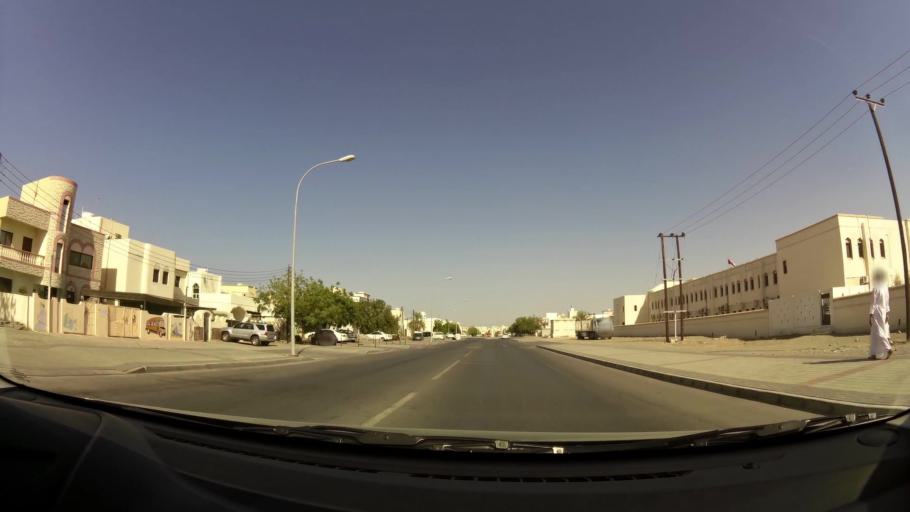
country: OM
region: Muhafazat Masqat
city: As Sib al Jadidah
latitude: 23.6286
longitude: 58.1985
